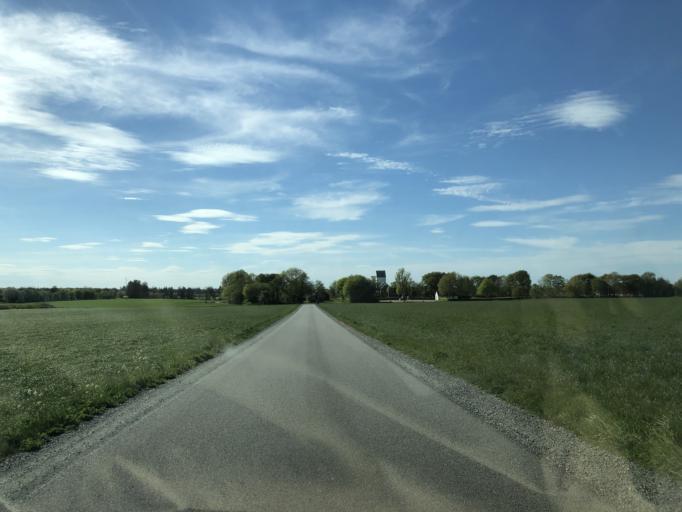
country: DK
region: Central Jutland
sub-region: Ringkobing-Skjern Kommune
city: Videbaek
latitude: 56.1718
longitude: 8.5259
